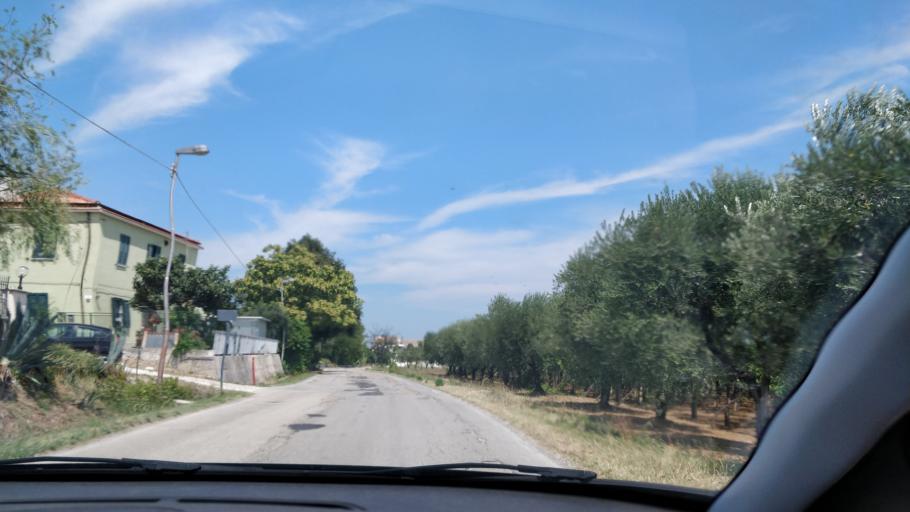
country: IT
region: Abruzzo
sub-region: Provincia di Chieti
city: Torrevecchia
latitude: 42.3951
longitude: 14.2000
